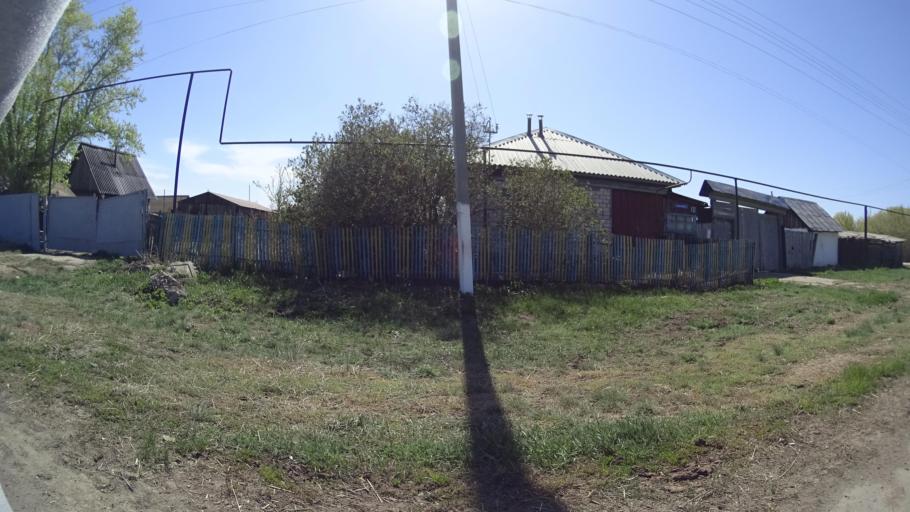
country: RU
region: Chelyabinsk
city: Chesma
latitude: 53.8008
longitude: 61.0186
